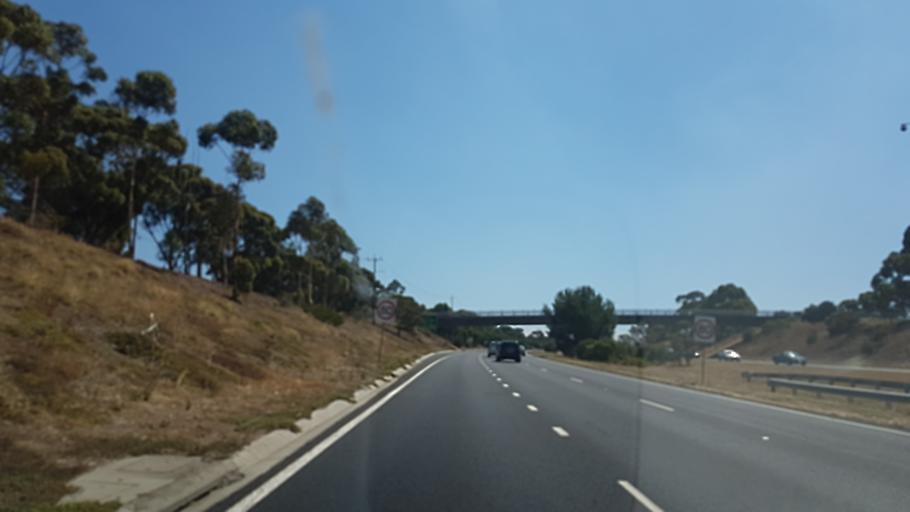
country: AU
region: Victoria
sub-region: Brimbank
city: Keilor
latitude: -37.7090
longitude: 144.8221
